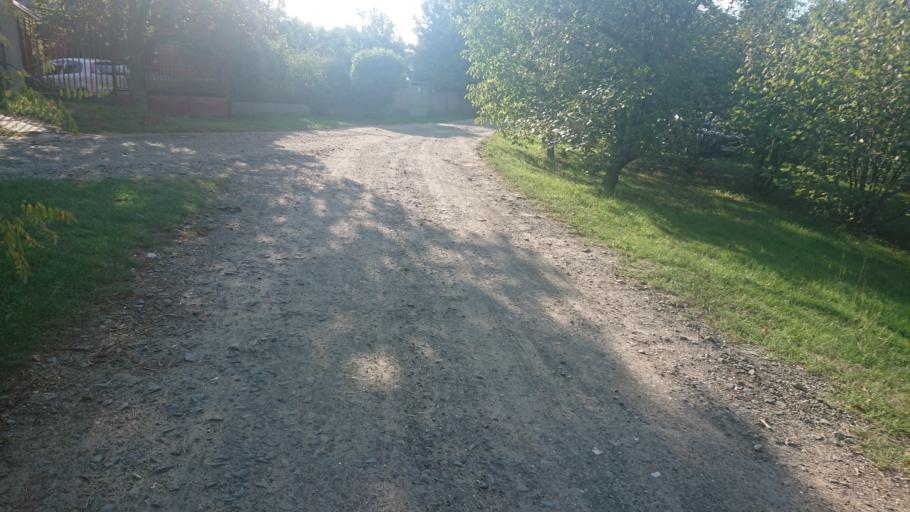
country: HU
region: Pest
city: Erdokertes
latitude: 47.6616
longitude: 19.3232
